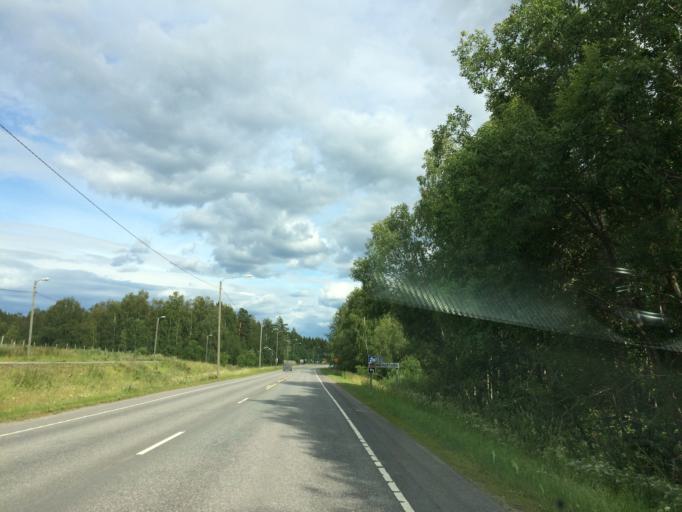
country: FI
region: Haeme
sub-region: Haemeenlinna
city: Janakkala
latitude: 60.9602
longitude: 24.5785
